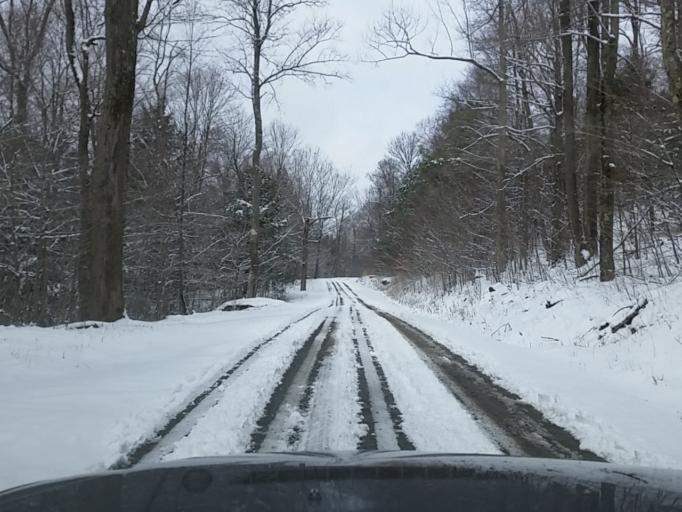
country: US
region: Pennsylvania
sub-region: Sullivan County
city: Laporte
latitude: 41.3439
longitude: -76.4635
